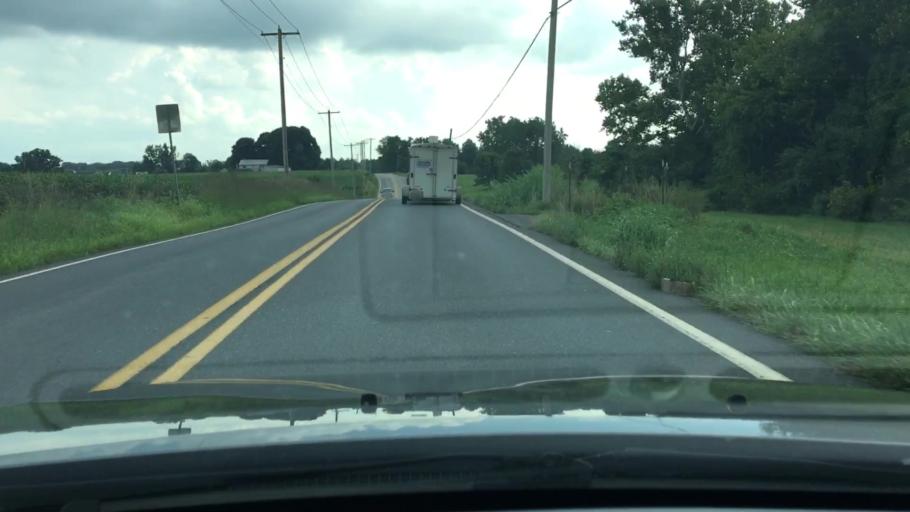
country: US
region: Pennsylvania
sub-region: Franklin County
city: Scotland
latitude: 39.9599
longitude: -77.5834
